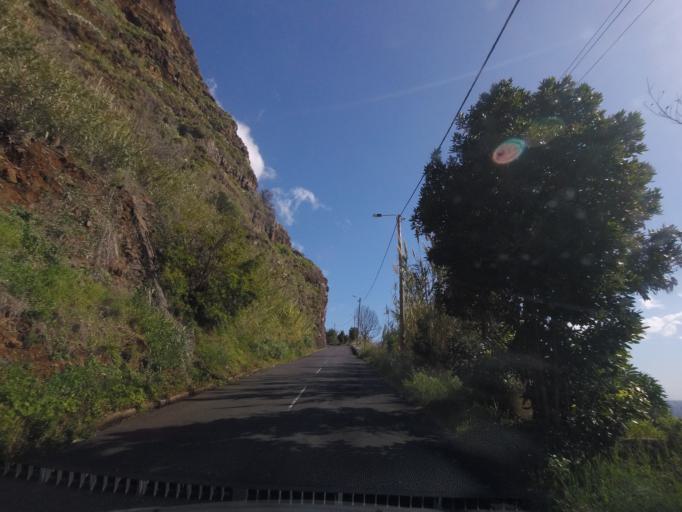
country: PT
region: Madeira
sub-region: Calheta
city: Estreito da Calheta
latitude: 32.7350
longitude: -17.2067
